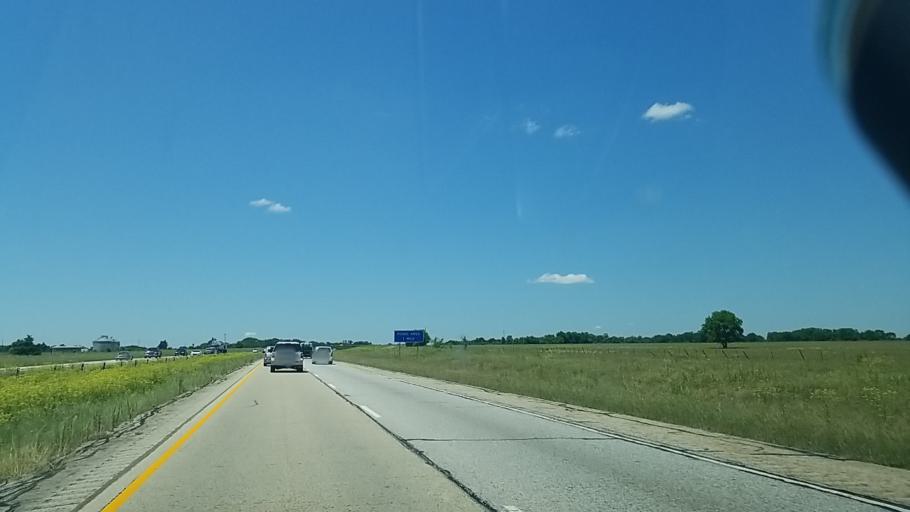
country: US
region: Texas
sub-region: Leon County
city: Centerville
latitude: 31.1190
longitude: -95.9738
